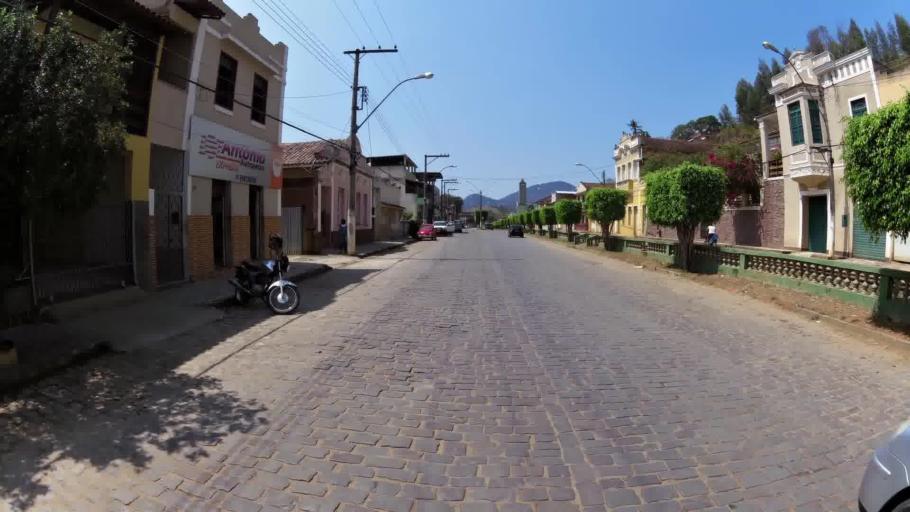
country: BR
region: Espirito Santo
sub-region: Mimoso Do Sul
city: Mimoso do Sul
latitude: -20.9492
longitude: -41.3423
